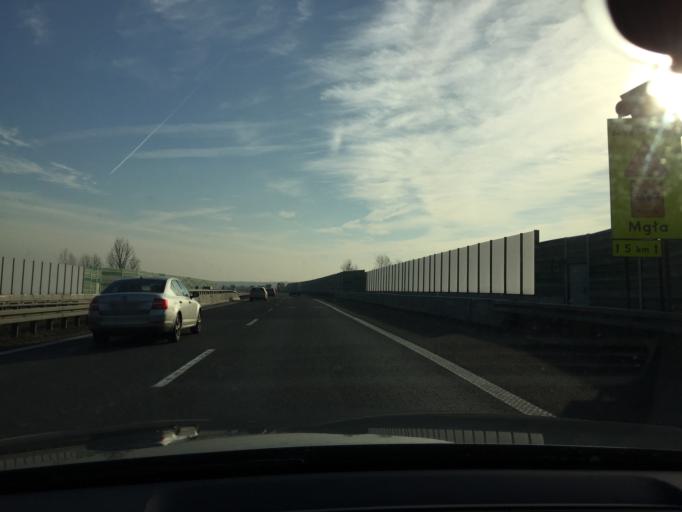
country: PL
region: Silesian Voivodeship
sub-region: Powiat gliwicki
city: Sosnicowice
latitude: 50.2756
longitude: 18.5748
